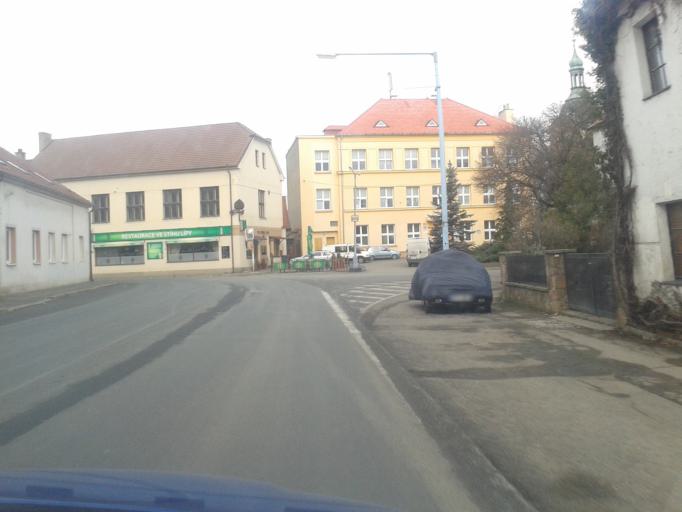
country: CZ
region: Central Bohemia
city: Revnice
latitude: 49.9045
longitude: 14.1473
